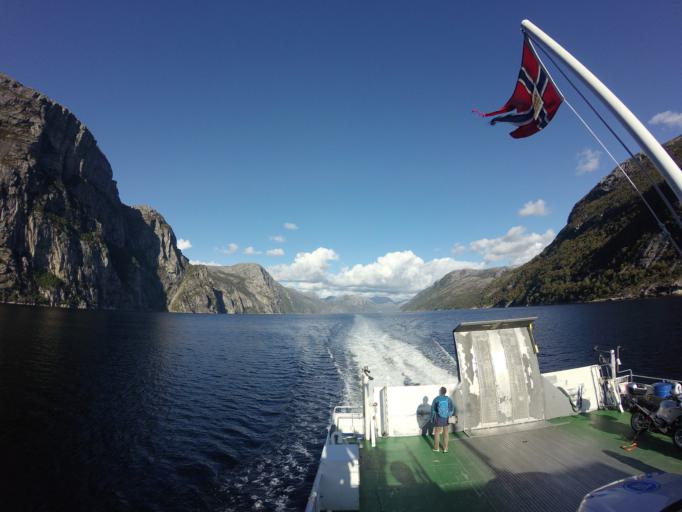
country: NO
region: Rogaland
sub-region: Forsand
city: Forsand
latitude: 58.9728
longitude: 6.1862
